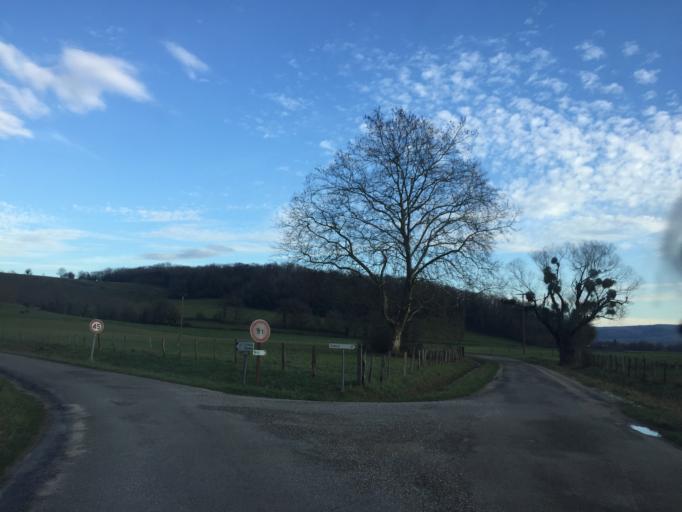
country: FR
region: Franche-Comte
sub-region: Departement du Jura
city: Arbois
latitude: 46.9323
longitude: 5.6866
